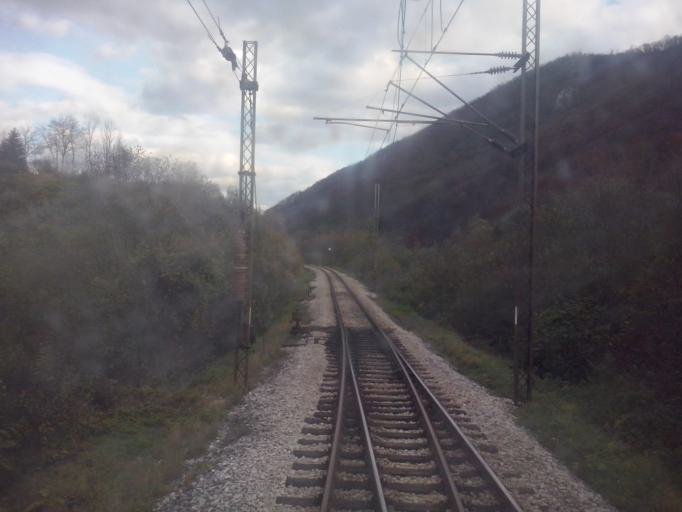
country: RS
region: Central Serbia
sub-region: Zlatiborski Okrug
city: Pozega
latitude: 43.8115
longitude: 19.9851
